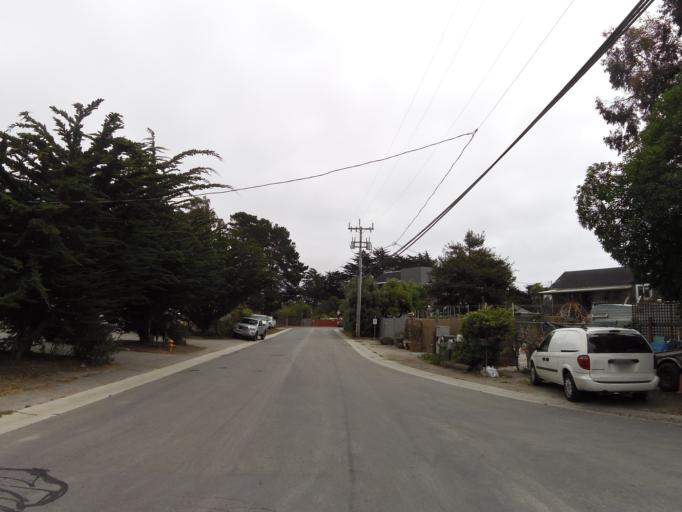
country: US
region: California
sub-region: San Mateo County
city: El Granada
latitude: 37.5054
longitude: -122.4888
